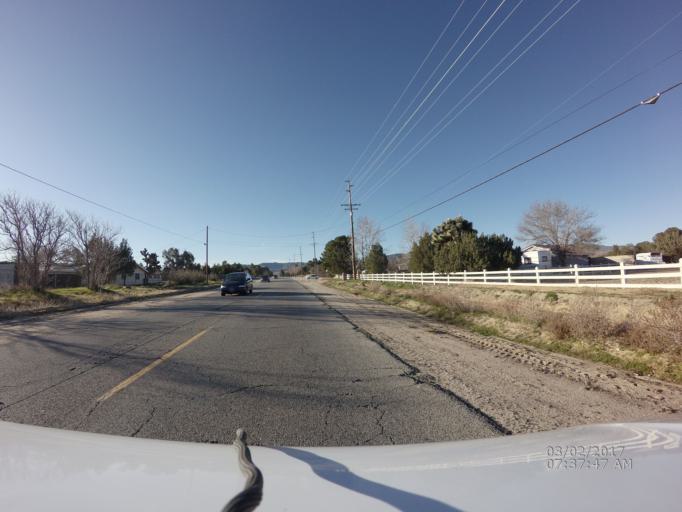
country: US
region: California
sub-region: Los Angeles County
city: Desert View Highlands
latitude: 34.6245
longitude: -118.1656
